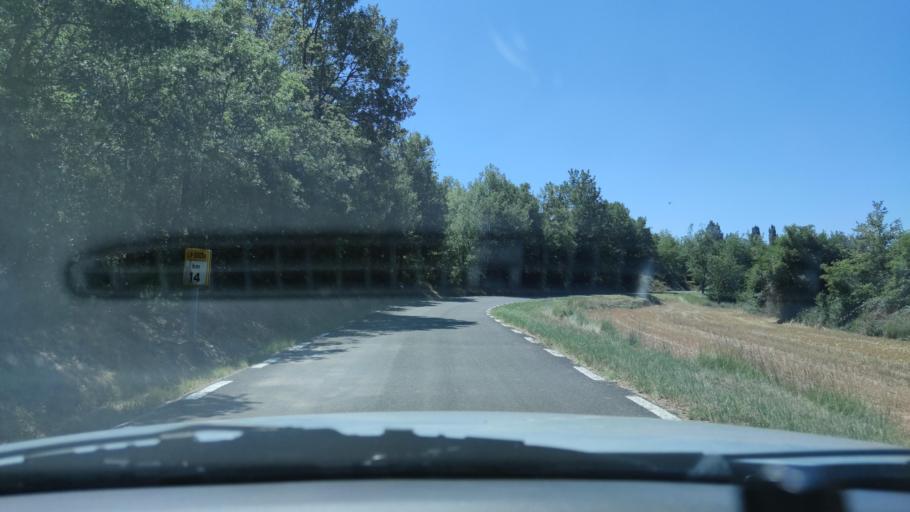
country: ES
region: Catalonia
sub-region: Provincia de Lleida
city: Tora de Riubregos
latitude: 41.8969
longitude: 1.4401
